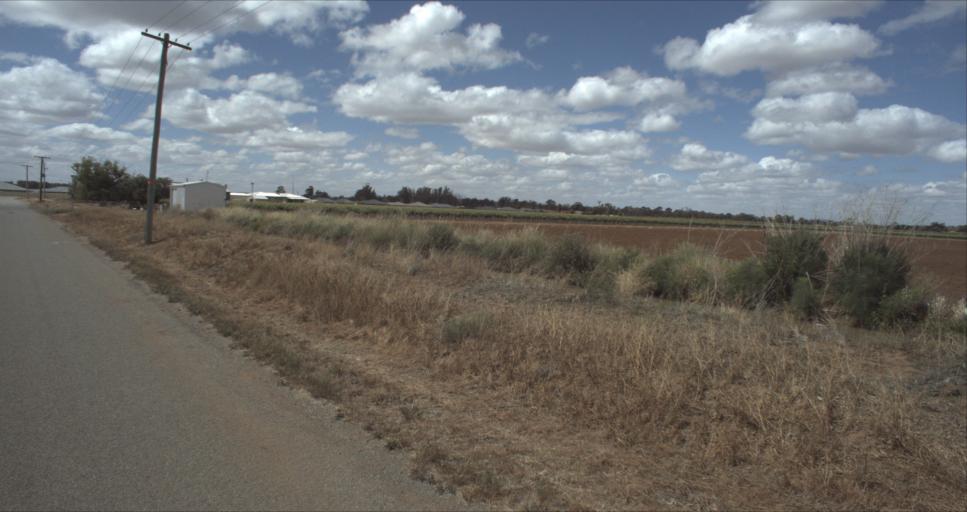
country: AU
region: New South Wales
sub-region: Leeton
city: Leeton
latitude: -34.5731
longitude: 146.3987
